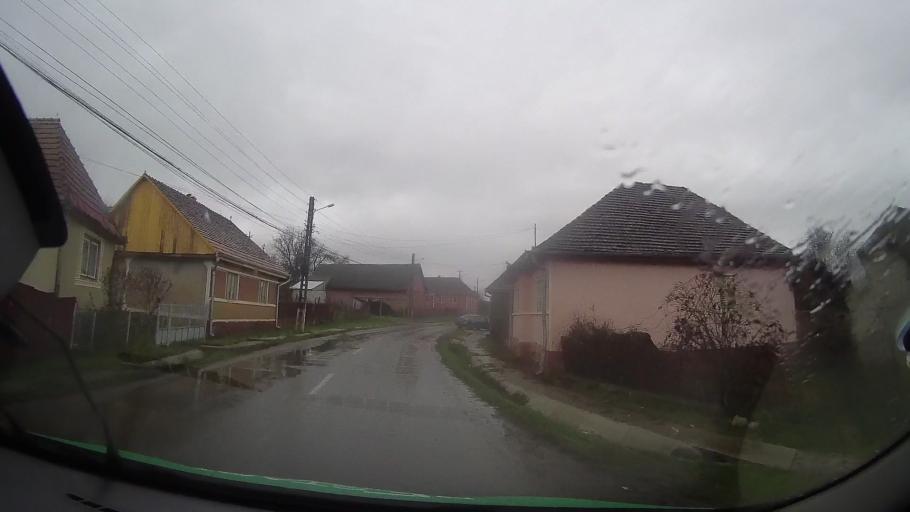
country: RO
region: Bistrita-Nasaud
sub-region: Comuna Monor
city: Monor
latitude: 46.9504
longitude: 24.7016
